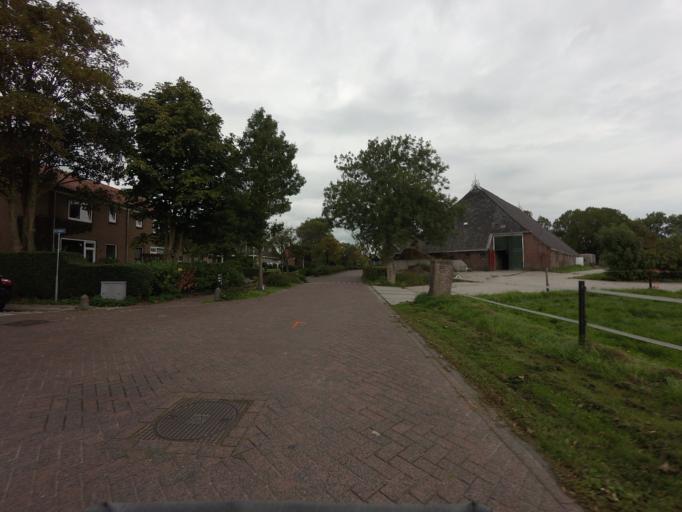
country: NL
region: Friesland
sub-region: Sudwest Fryslan
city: IJlst
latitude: 53.0155
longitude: 5.6031
